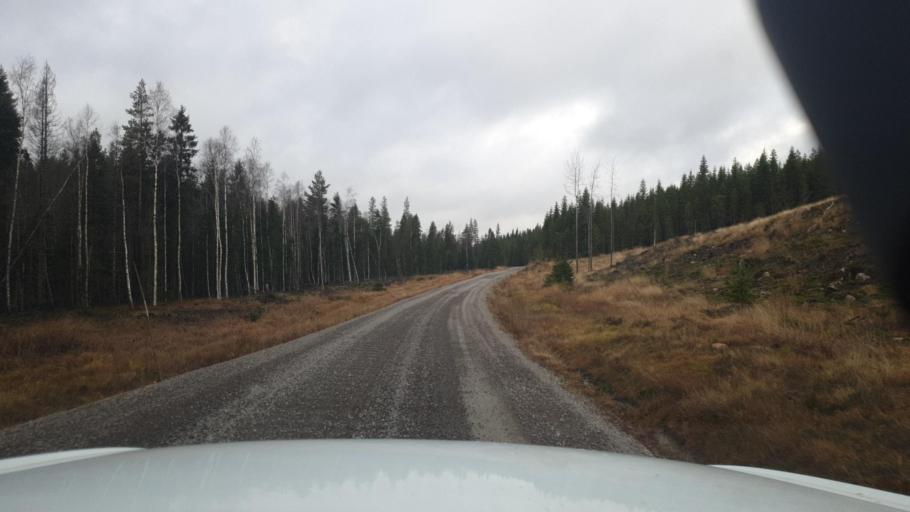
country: SE
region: Vaermland
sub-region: Eda Kommun
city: Charlottenberg
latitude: 60.0737
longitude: 12.6208
